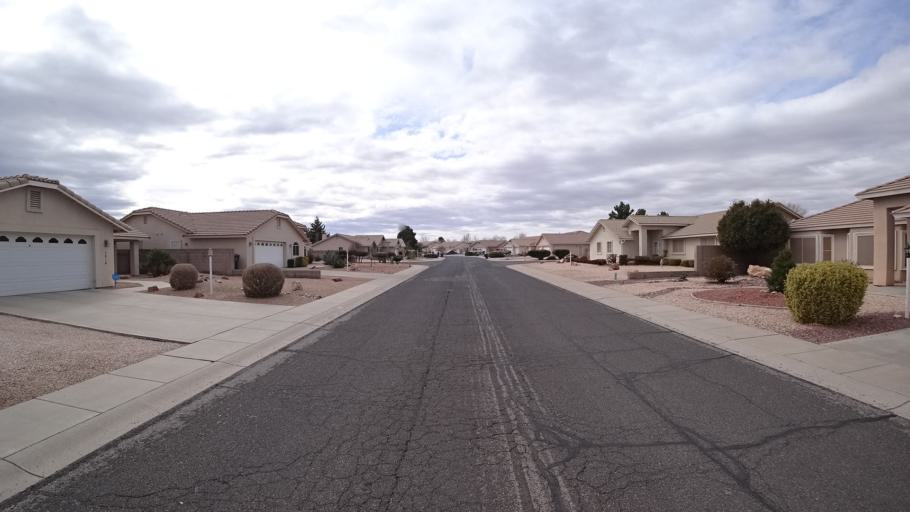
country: US
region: Arizona
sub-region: Mohave County
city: New Kingman-Butler
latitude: 35.2341
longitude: -114.0302
